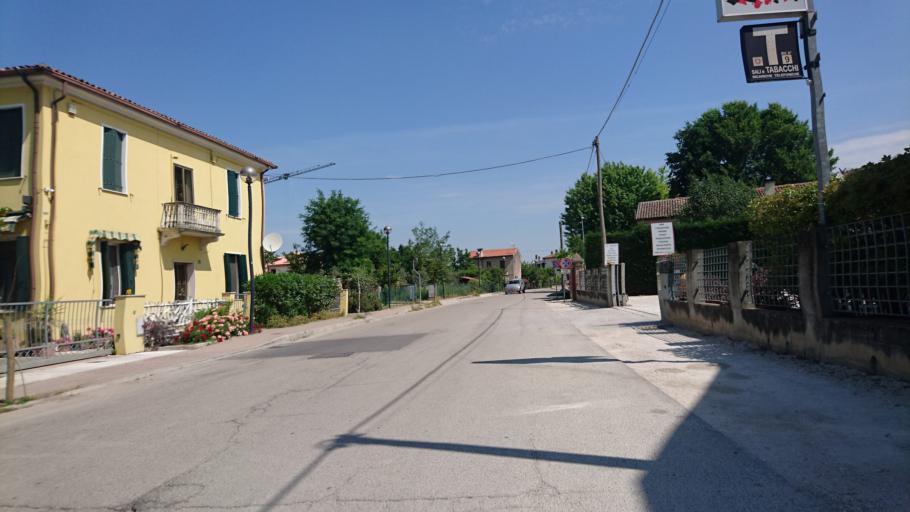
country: IT
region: Veneto
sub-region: Provincia di Padova
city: Ospedaletto Euganeo
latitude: 45.2184
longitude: 11.6037
